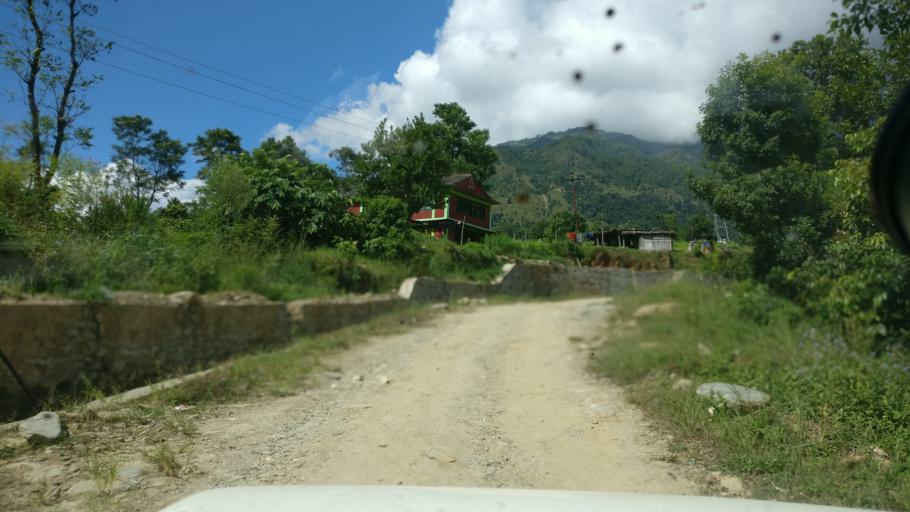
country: NP
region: Western Region
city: Baglung
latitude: 28.2497
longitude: 83.6505
